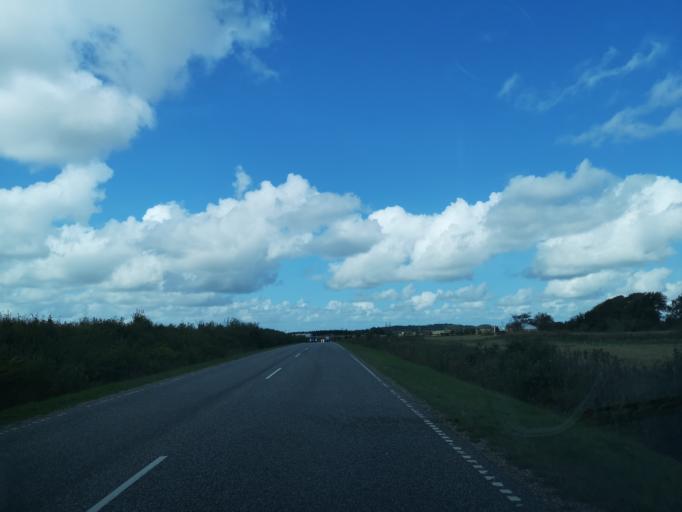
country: DK
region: Central Jutland
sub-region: Holstebro Kommune
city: Holstebro
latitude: 56.3902
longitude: 8.5935
